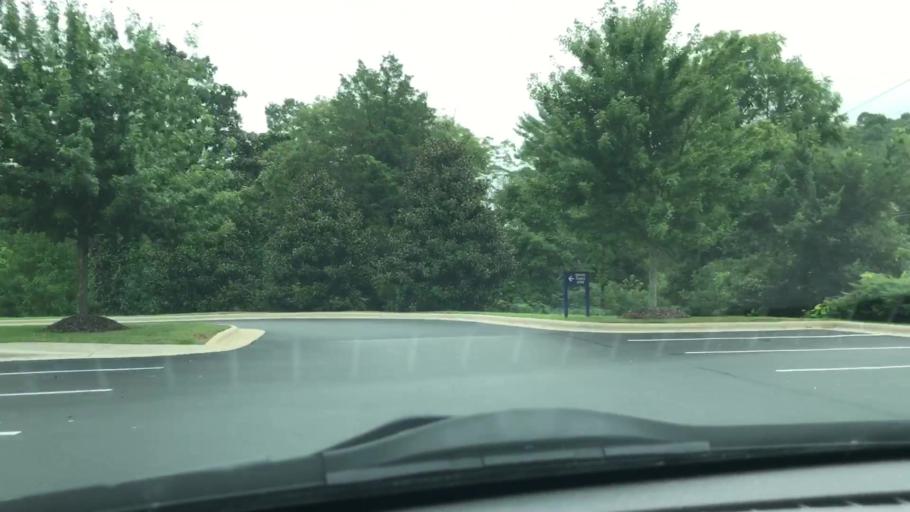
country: US
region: North Carolina
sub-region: Randolph County
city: Randleman
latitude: 35.8183
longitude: -79.8095
